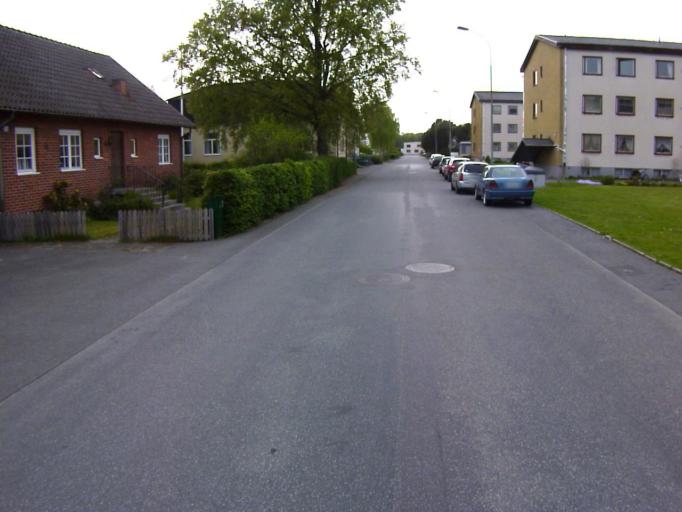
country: SE
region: Skane
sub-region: Kristianstads Kommun
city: Onnestad
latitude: 55.9336
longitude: 13.9729
